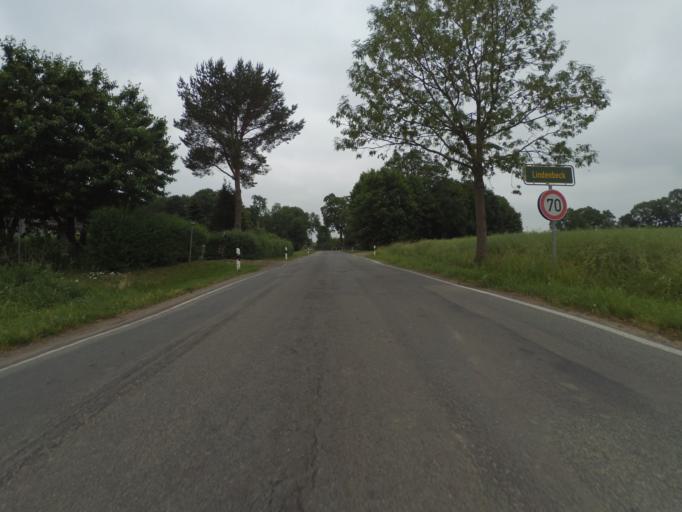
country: DE
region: Mecklenburg-Vorpommern
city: Lubz
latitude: 53.4957
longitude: 11.9677
